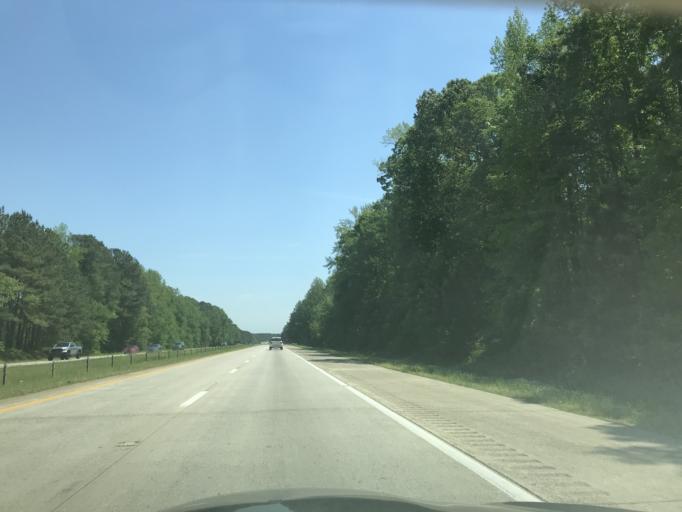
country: US
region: North Carolina
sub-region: Johnston County
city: Benson
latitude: 35.5302
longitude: -78.5679
